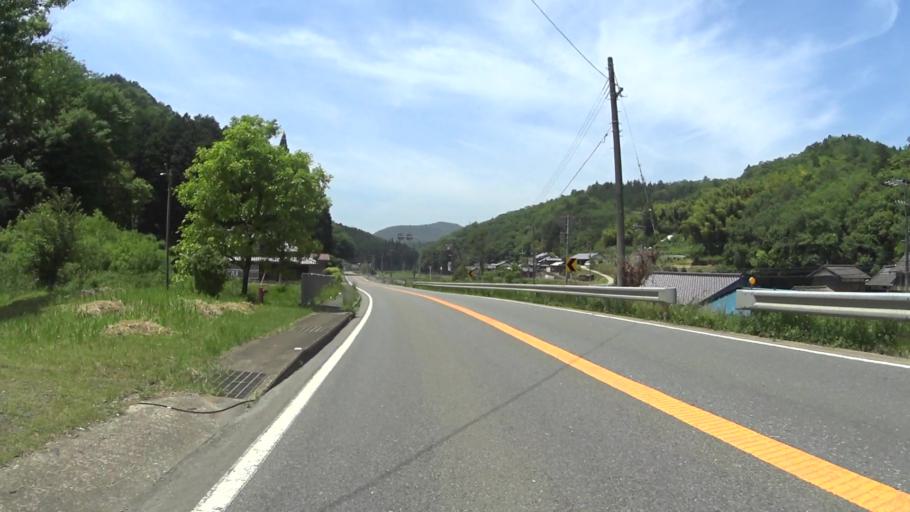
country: JP
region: Kyoto
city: Ayabe
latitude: 35.1833
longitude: 135.3437
